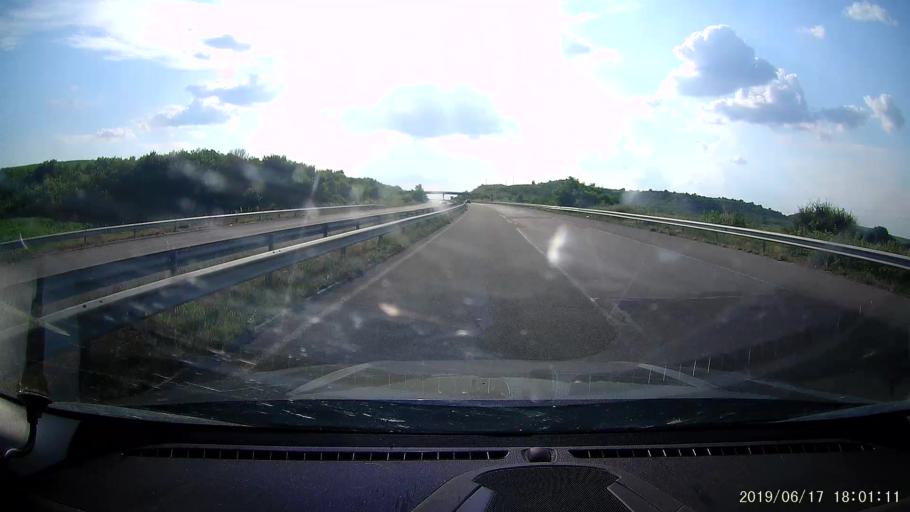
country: BG
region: Khaskovo
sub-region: Obshtina Svilengrad
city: Svilengrad
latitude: 41.7445
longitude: 26.2620
